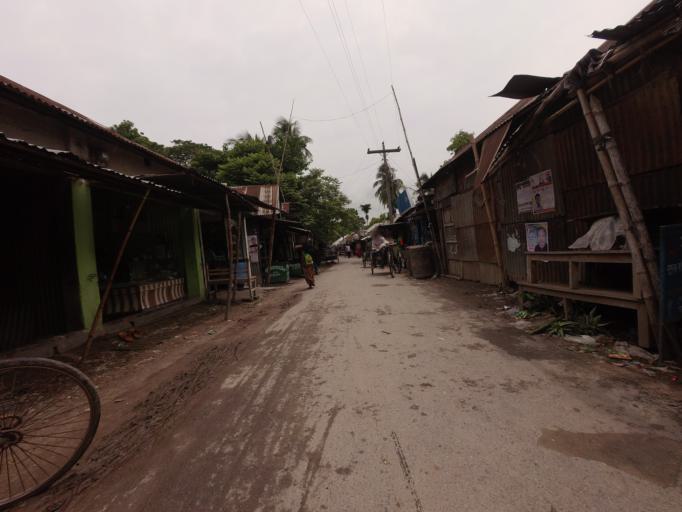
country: BD
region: Khulna
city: Kalia
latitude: 23.0848
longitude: 89.6707
